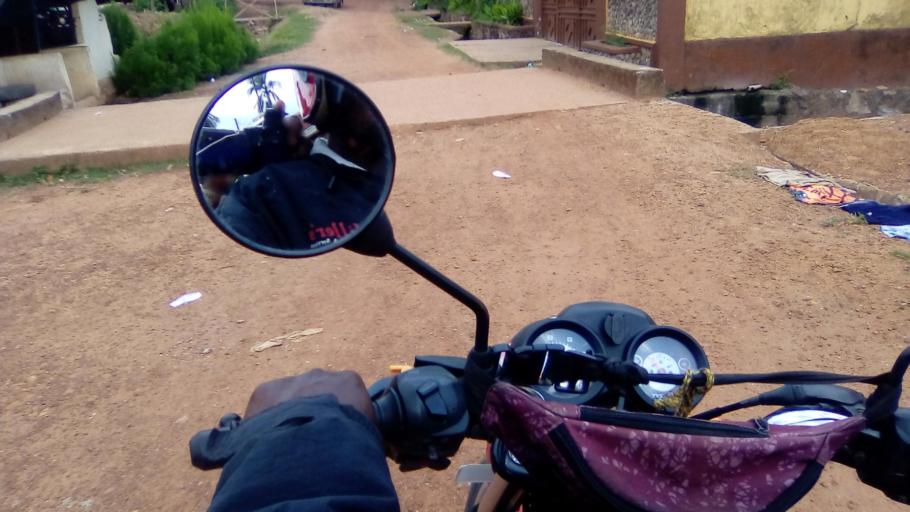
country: SL
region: Southern Province
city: Bo
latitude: 7.9582
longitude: -11.7306
